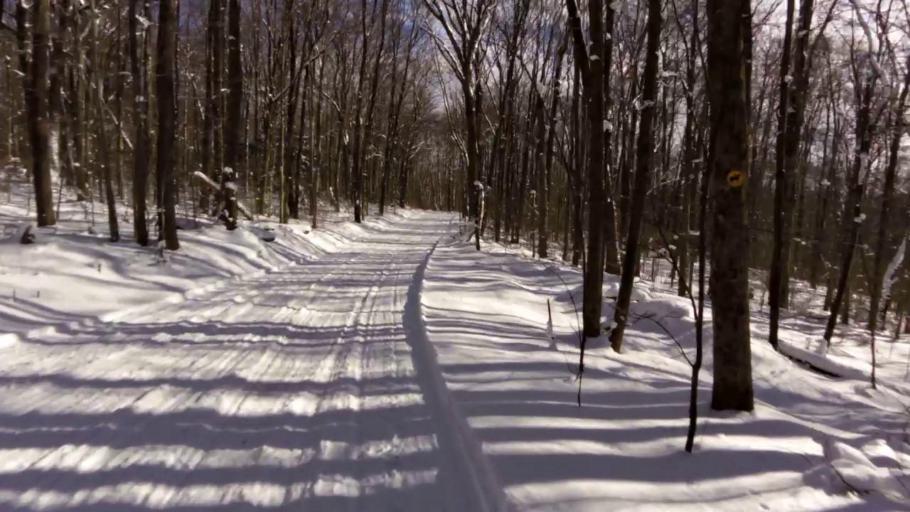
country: US
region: New York
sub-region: Cattaraugus County
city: Salamanca
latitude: 42.0742
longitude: -78.6870
